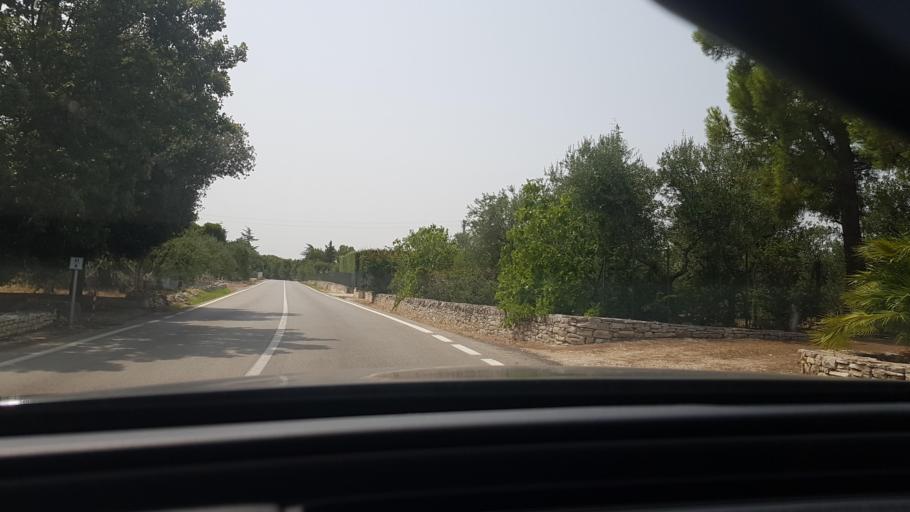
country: IT
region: Apulia
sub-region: Provincia di Barletta - Andria - Trani
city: Andria
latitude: 41.1308
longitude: 16.2902
